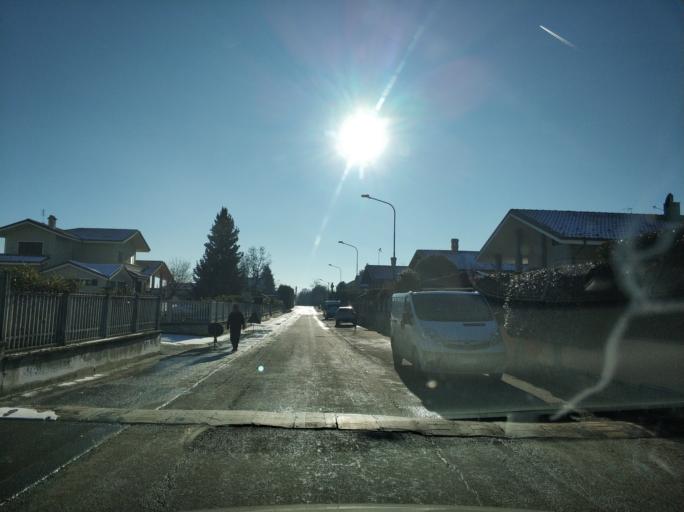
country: IT
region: Piedmont
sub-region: Provincia di Torino
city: San Maurizio
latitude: 45.2384
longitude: 7.6353
